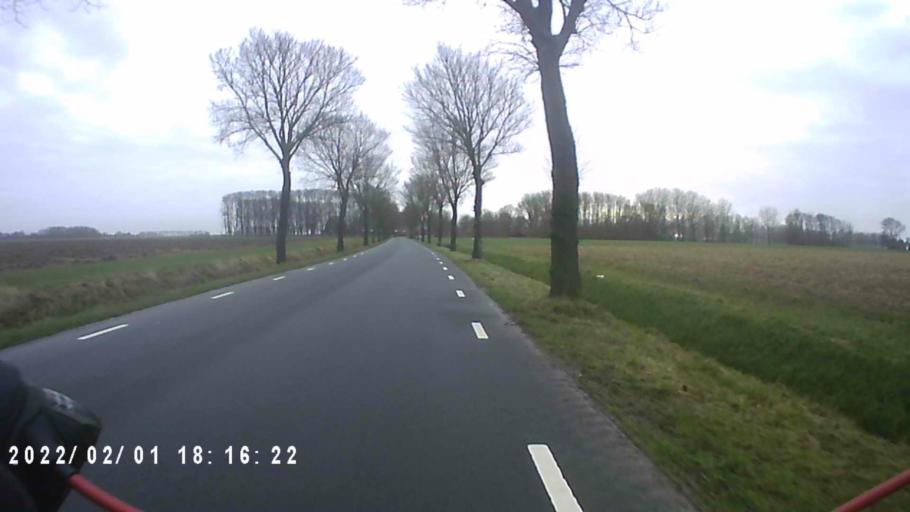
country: NL
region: Groningen
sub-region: Gemeente De Marne
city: Ulrum
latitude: 53.3459
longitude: 6.3319
